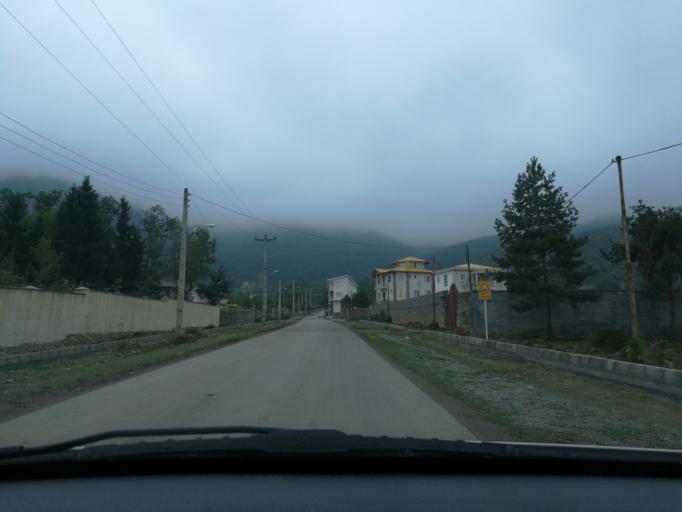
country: IR
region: Mazandaran
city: `Abbasabad
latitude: 36.4992
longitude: 51.2156
